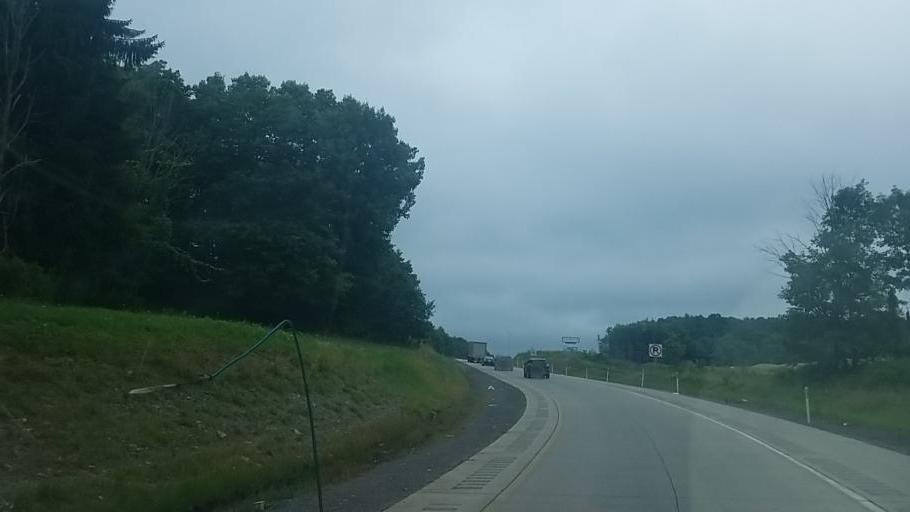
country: US
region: Pennsylvania
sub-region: Jefferson County
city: Brookville
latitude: 41.1695
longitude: -79.0964
